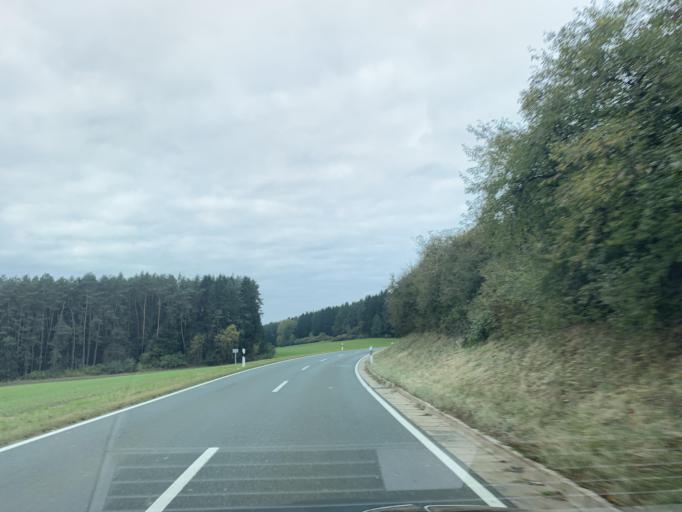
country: DE
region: Bavaria
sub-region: Upper Franconia
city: Pottenstein
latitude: 49.7284
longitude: 11.4514
